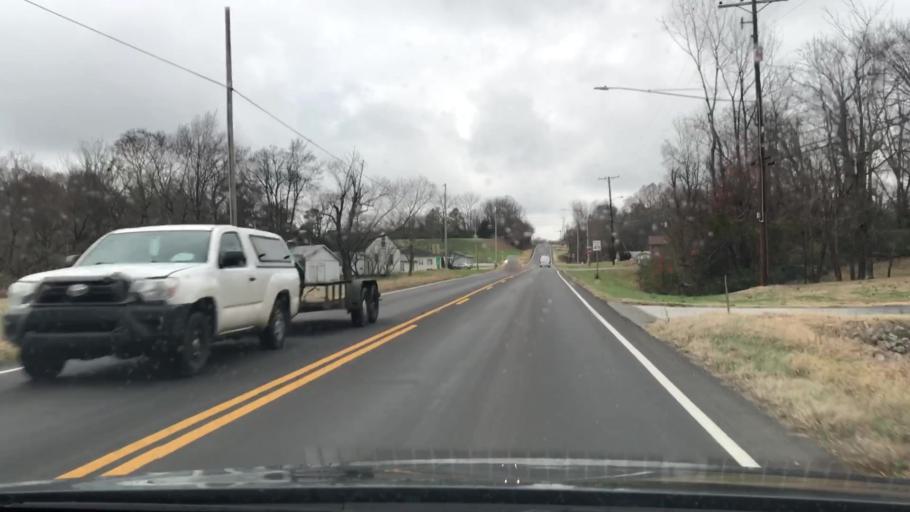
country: US
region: Kentucky
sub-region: Christian County
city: Hopkinsville
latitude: 36.8640
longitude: -87.4602
